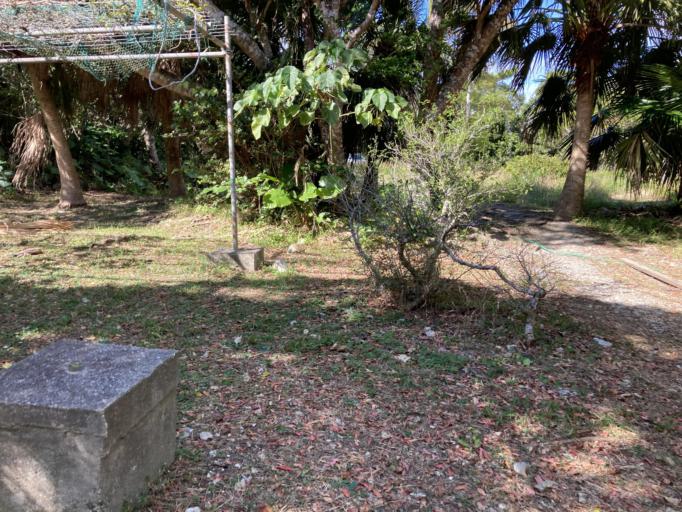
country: JP
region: Okinawa
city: Tomigusuku
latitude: 26.1439
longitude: 127.7820
